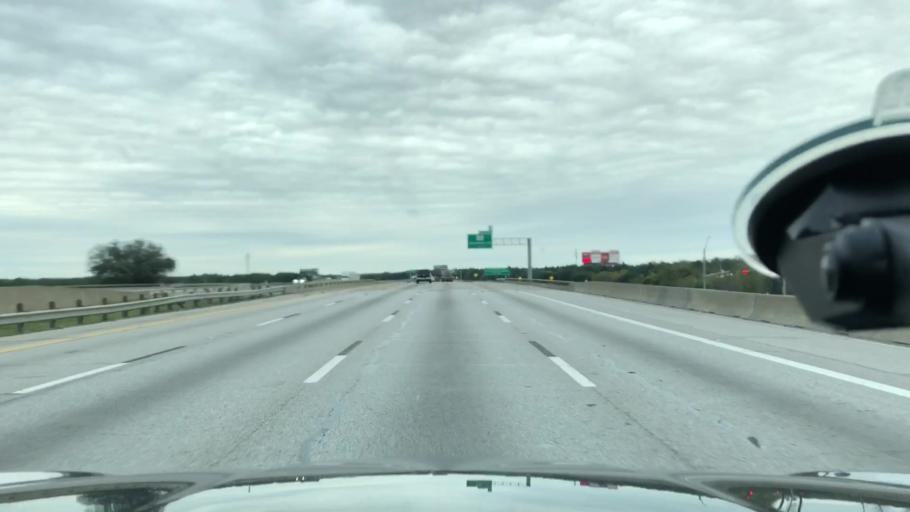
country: US
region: Texas
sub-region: Dallas County
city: Lancaster
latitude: 32.6421
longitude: -96.8069
